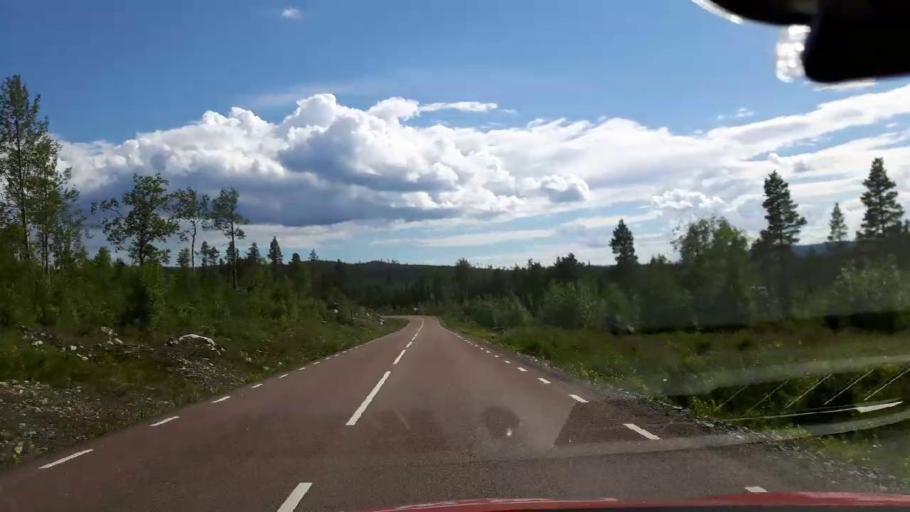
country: SE
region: Jaemtland
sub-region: Krokoms Kommun
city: Valla
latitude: 64.0351
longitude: 14.1913
